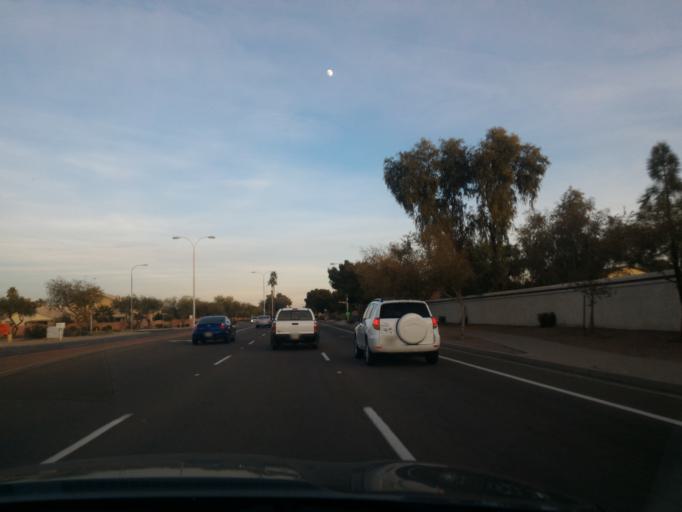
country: US
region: Arizona
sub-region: Maricopa County
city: Guadalupe
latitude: 33.3054
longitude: -111.9249
